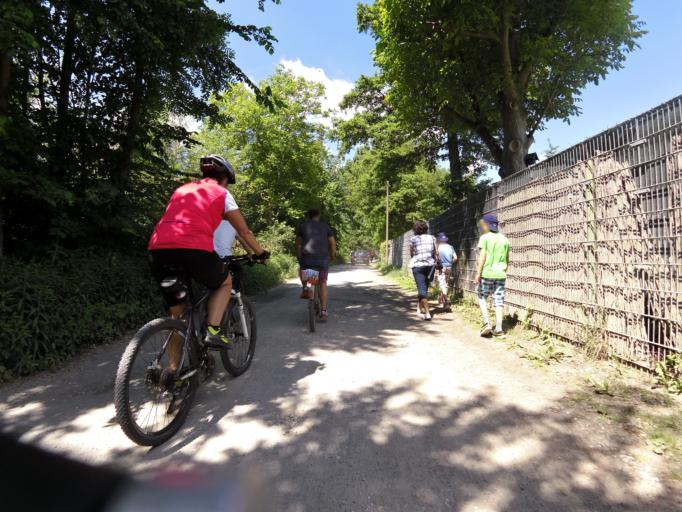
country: DE
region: Rheinland-Pfalz
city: Nackenheim
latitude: 49.9223
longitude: 8.3543
